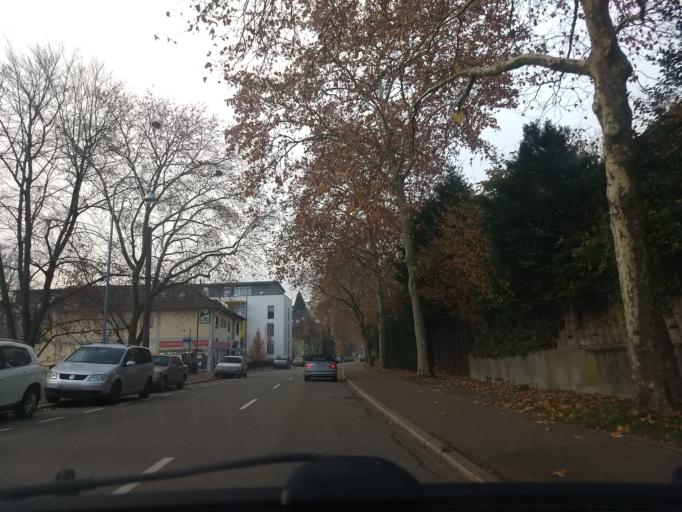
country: DE
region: Baden-Wuerttemberg
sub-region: Karlsruhe Region
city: Baden-Baden
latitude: 48.7801
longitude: 8.2129
